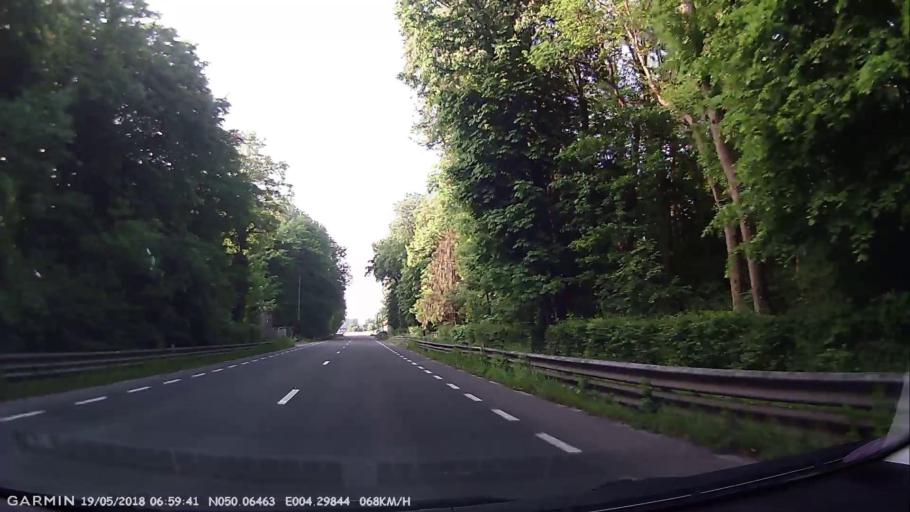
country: BE
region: Wallonia
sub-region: Province du Hainaut
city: Chimay
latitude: 50.0644
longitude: 4.2986
